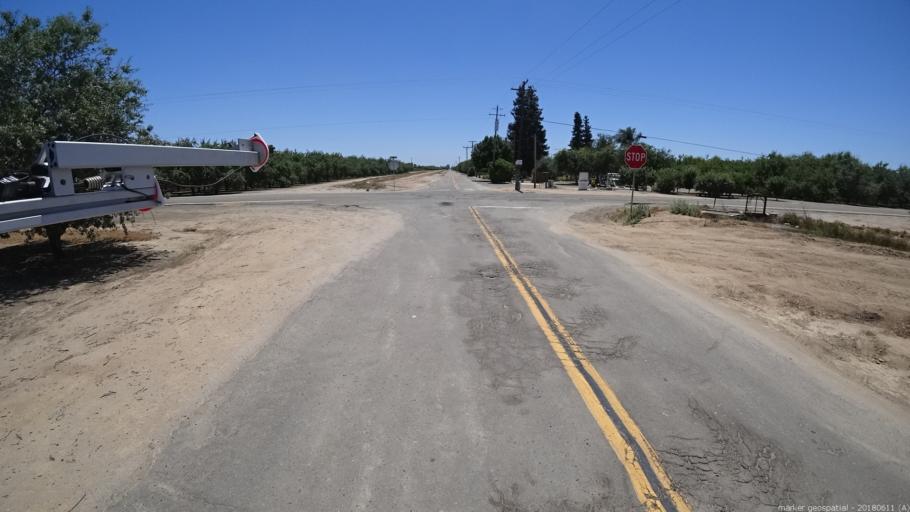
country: US
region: California
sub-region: Madera County
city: Fairmead
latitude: 37.0403
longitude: -120.1932
